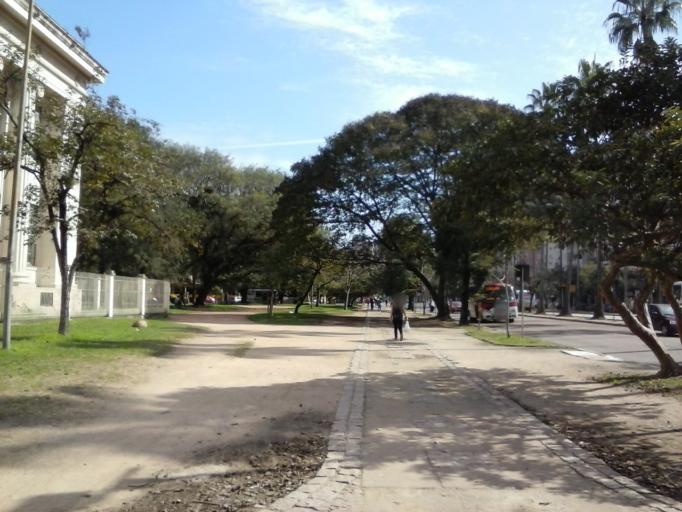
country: BR
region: Rio Grande do Sul
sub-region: Porto Alegre
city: Porto Alegre
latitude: -30.0332
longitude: -51.2175
